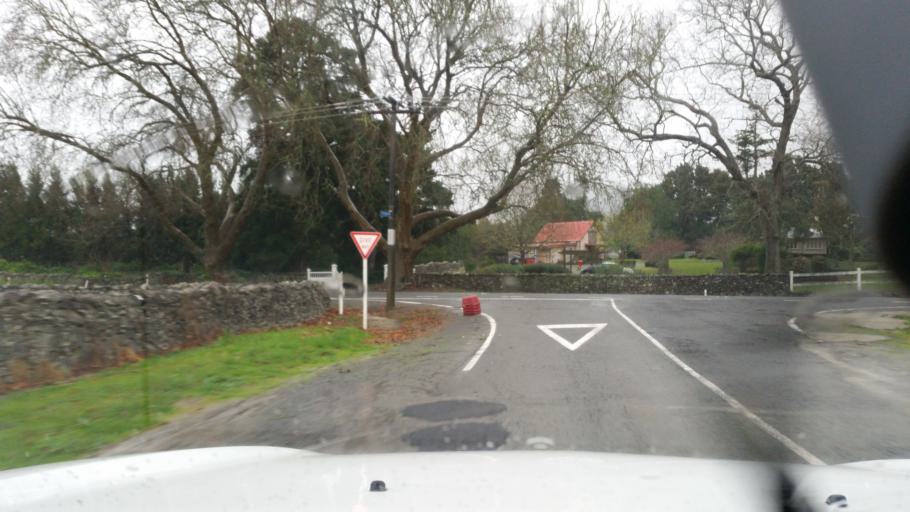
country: NZ
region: Northland
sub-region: Whangarei
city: Maungatapere
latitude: -35.7547
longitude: 174.1831
